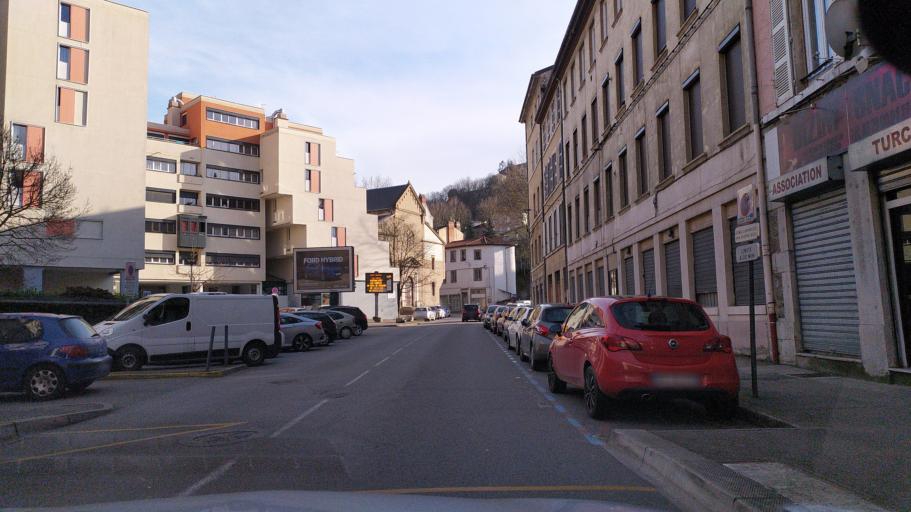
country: FR
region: Rhone-Alpes
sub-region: Departement de l'Isere
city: Vienne
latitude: 45.5290
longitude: 4.8780
